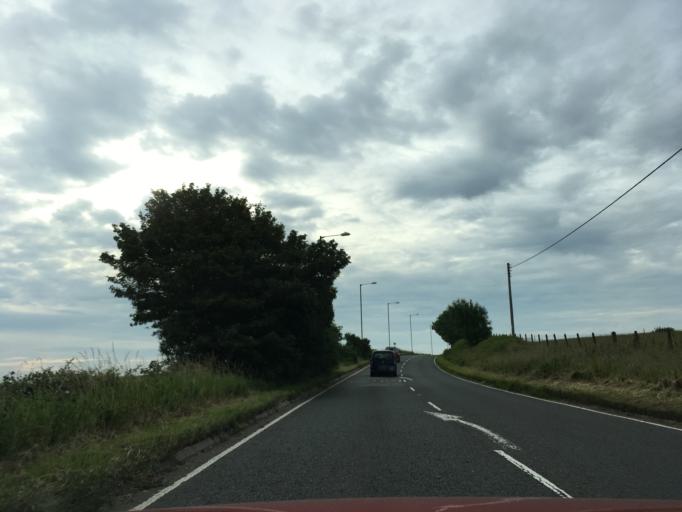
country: GB
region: England
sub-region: North Somerset
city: Easton-in-Gordano
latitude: 51.4708
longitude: -2.6867
